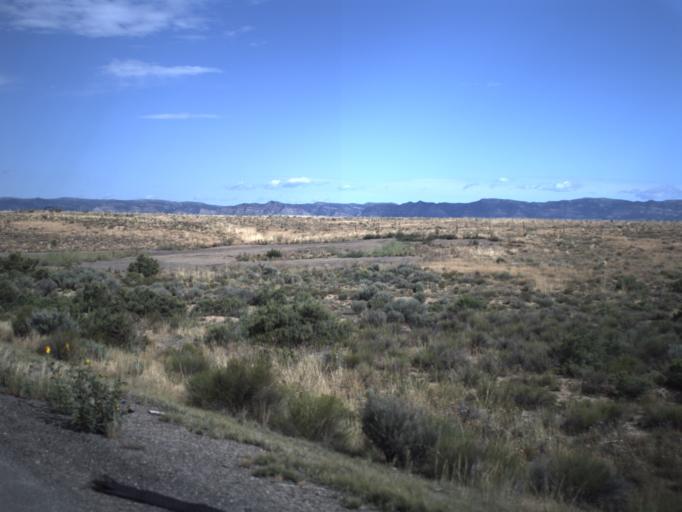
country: US
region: Utah
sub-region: Carbon County
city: East Carbon City
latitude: 39.5112
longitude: -110.5395
